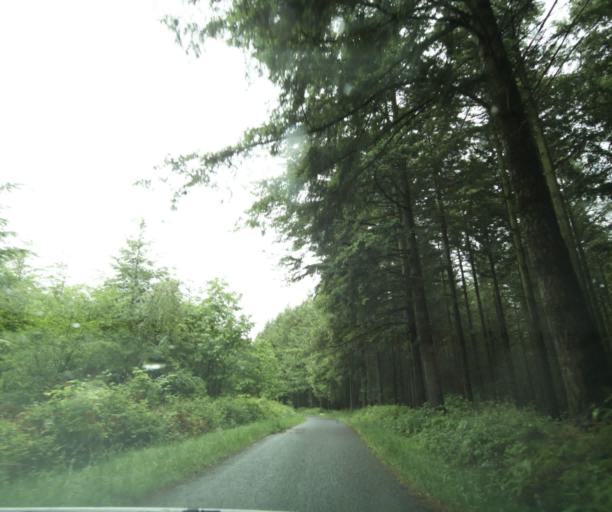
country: FR
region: Bourgogne
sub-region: Departement de Saone-et-Loire
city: Palinges
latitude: 46.5367
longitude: 4.2643
